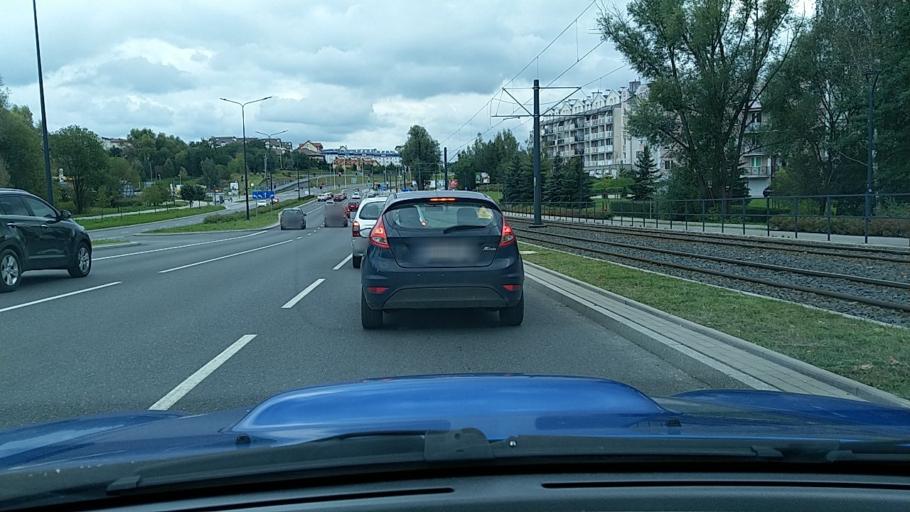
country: PL
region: Warmian-Masurian Voivodeship
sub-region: Olsztyn
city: Kortowo
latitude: 53.7422
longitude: 20.4862
